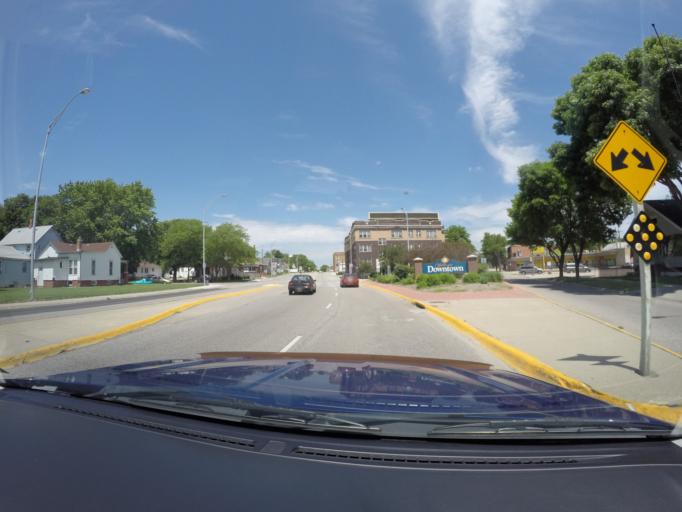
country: US
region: Nebraska
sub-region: Hall County
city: Grand Island
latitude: 40.9198
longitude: -98.3399
